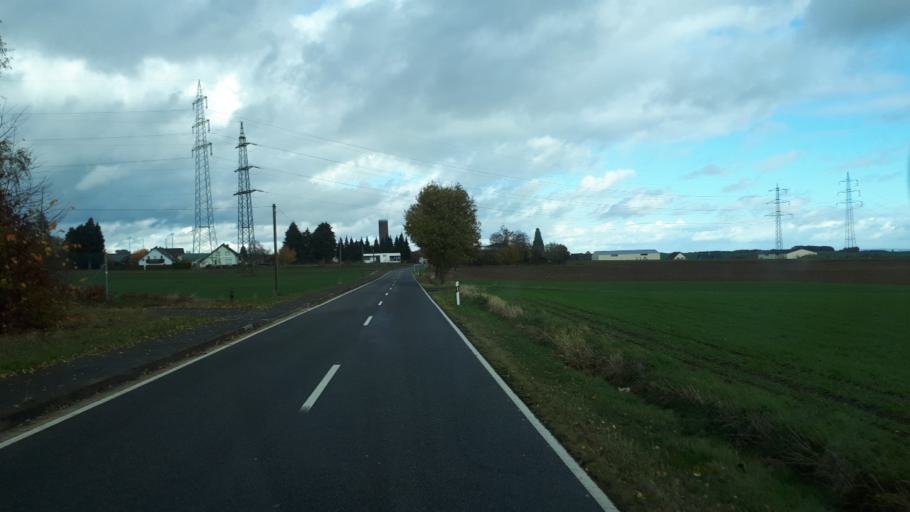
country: DE
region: Rheinland-Pfalz
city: Binningen
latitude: 50.2137
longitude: 7.2499
